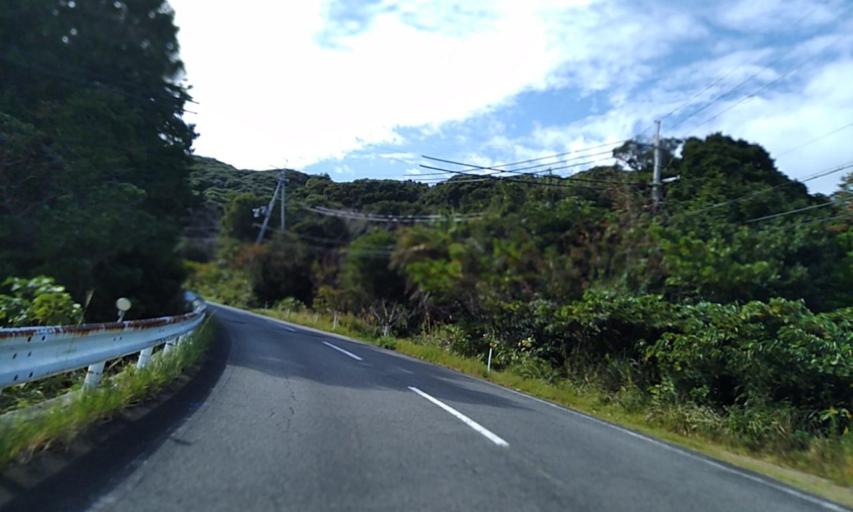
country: JP
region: Wakayama
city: Shingu
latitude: 33.4699
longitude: 135.8356
